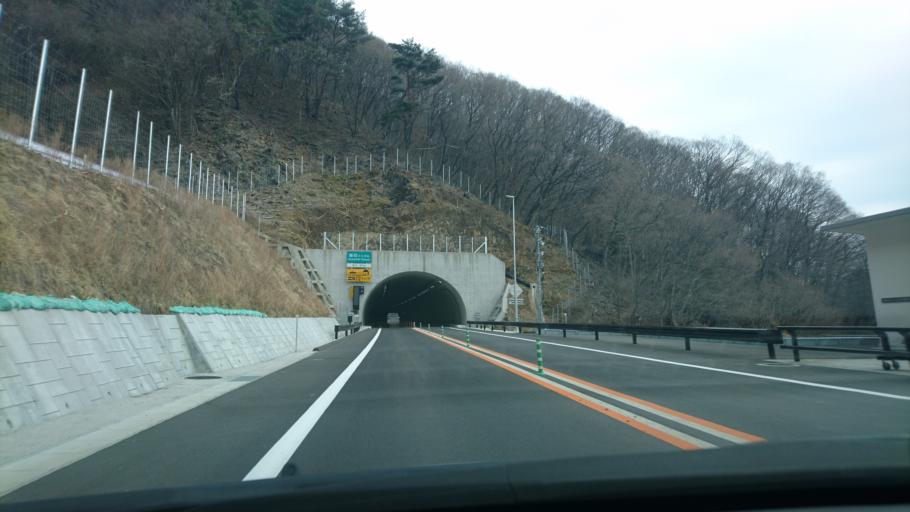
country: JP
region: Iwate
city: Kamaishi
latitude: 39.2669
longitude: 141.8455
